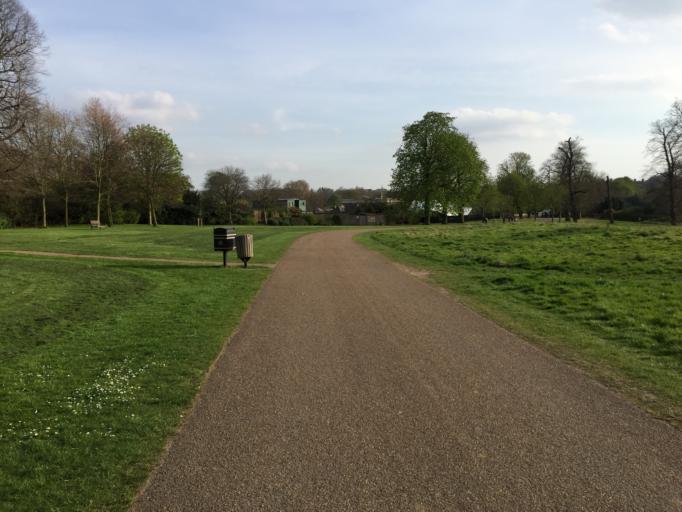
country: GB
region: England
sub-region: Greater London
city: Bayswater
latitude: 51.5087
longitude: -0.1712
